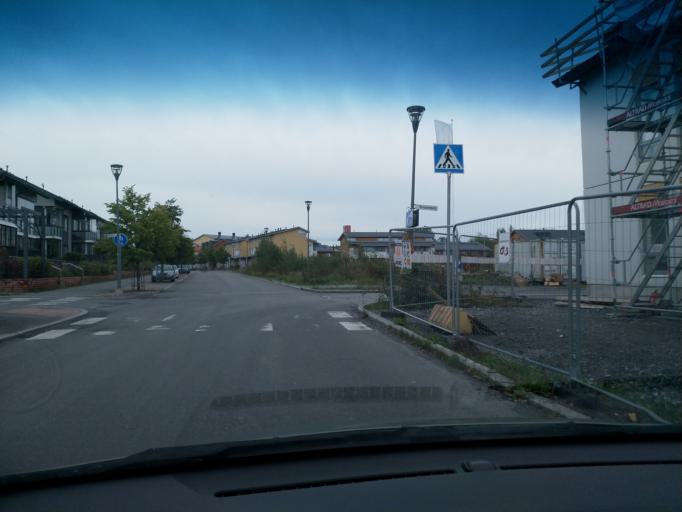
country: FI
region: Pirkanmaa
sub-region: Tampere
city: Tampere
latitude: 61.4768
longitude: 23.8285
